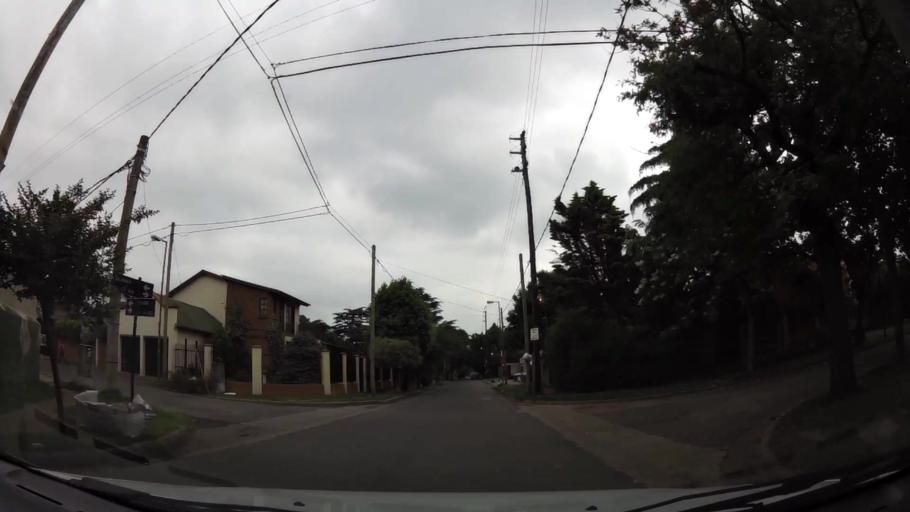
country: AR
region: Buenos Aires
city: San Justo
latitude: -34.7350
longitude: -58.5279
